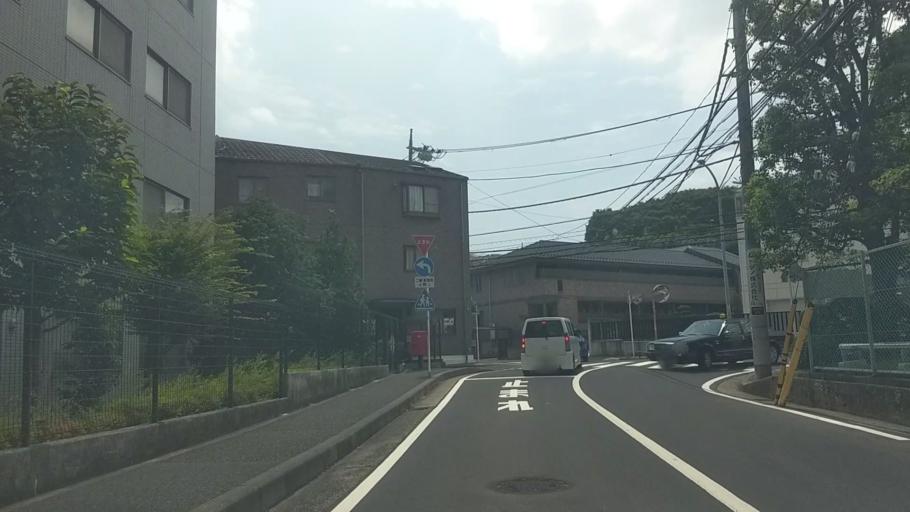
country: JP
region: Kanagawa
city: Yokohama
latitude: 35.5128
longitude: 139.6299
